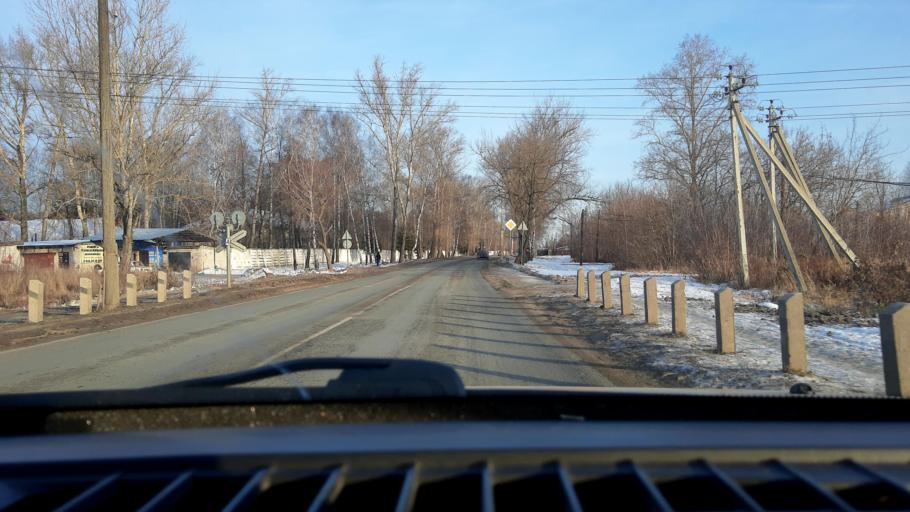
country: RU
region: Nizjnij Novgorod
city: Bor
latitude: 56.3787
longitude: 44.0320
